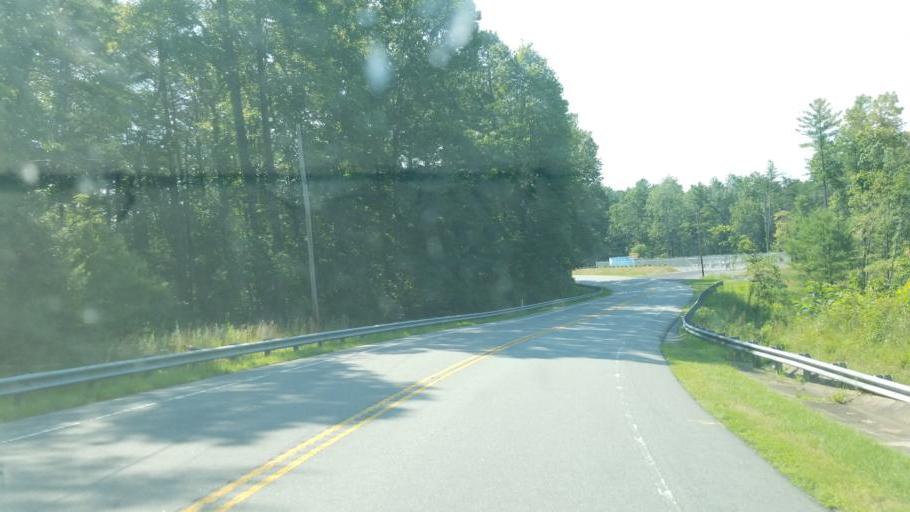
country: US
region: North Carolina
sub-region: Burke County
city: Glen Alpine
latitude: 35.8822
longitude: -81.7966
